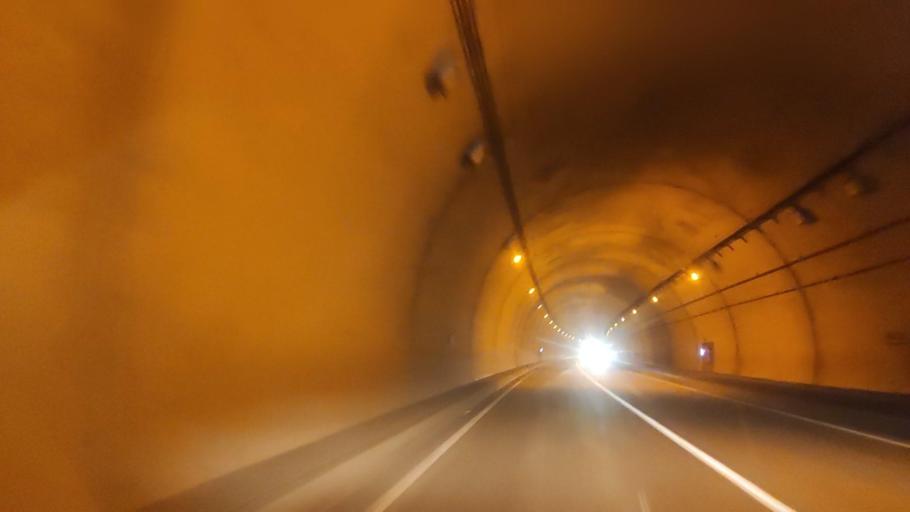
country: JP
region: Hokkaido
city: Date
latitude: 42.5613
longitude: 140.7809
